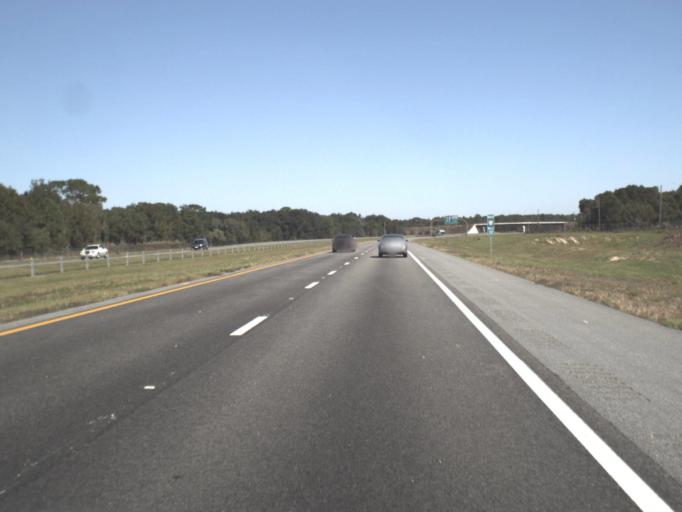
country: US
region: Florida
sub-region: Pasco County
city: Shady Hills
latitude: 28.3791
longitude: -82.5406
